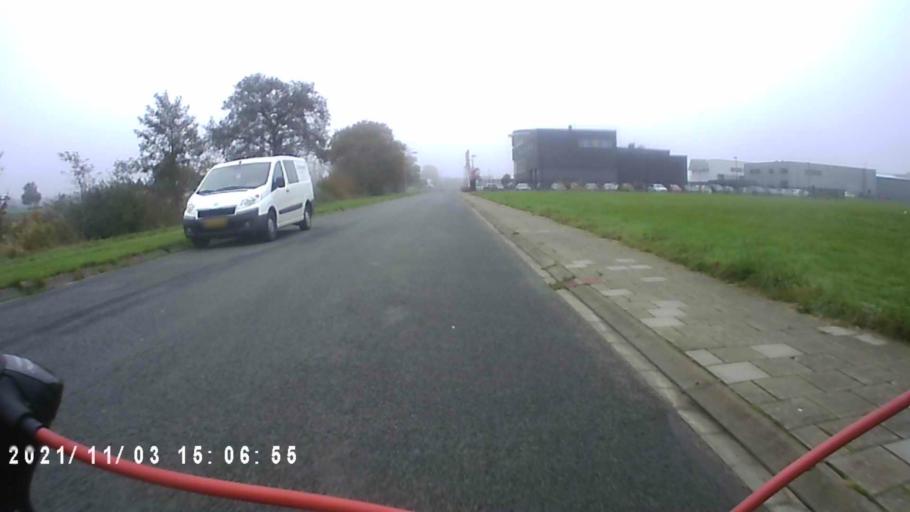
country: NL
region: Groningen
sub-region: Gemeente Leek
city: Leek
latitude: 53.1843
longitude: 6.3707
